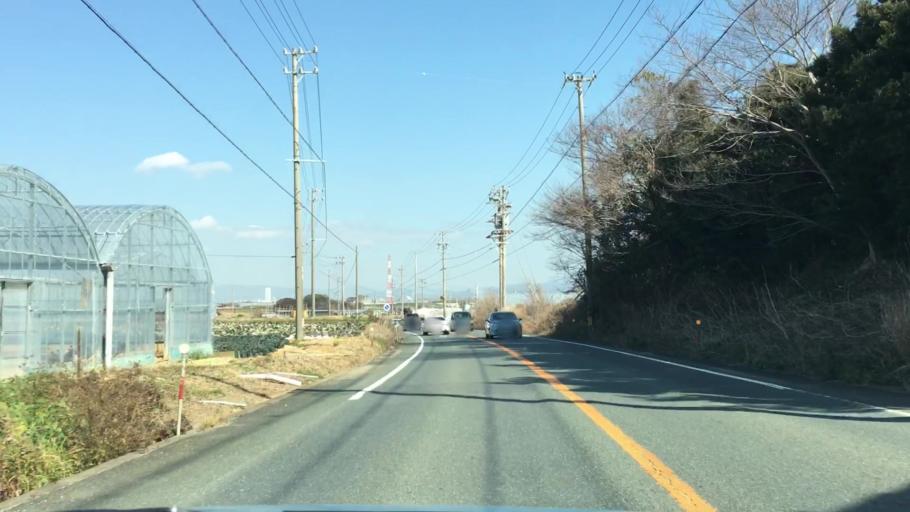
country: JP
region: Aichi
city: Toyohashi
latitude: 34.6994
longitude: 137.3440
